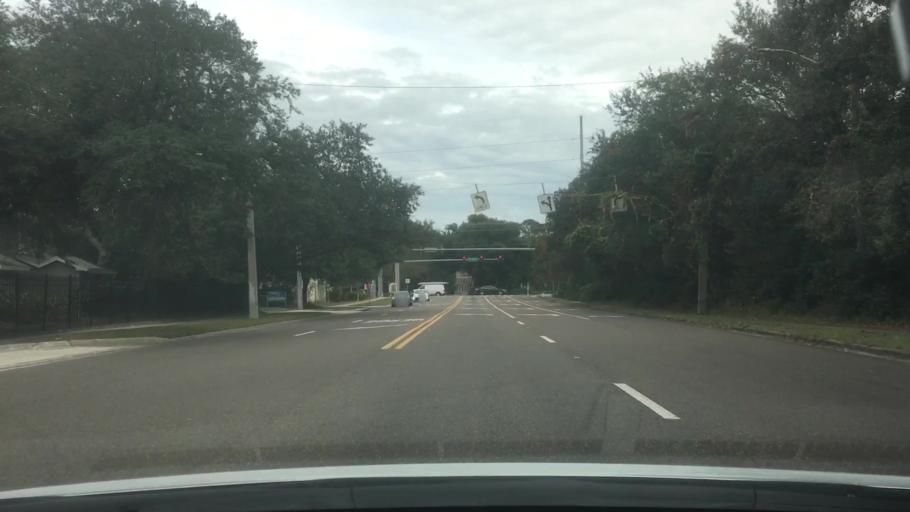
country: US
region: Florida
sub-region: Duval County
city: Atlantic Beach
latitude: 30.3537
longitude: -81.4152
